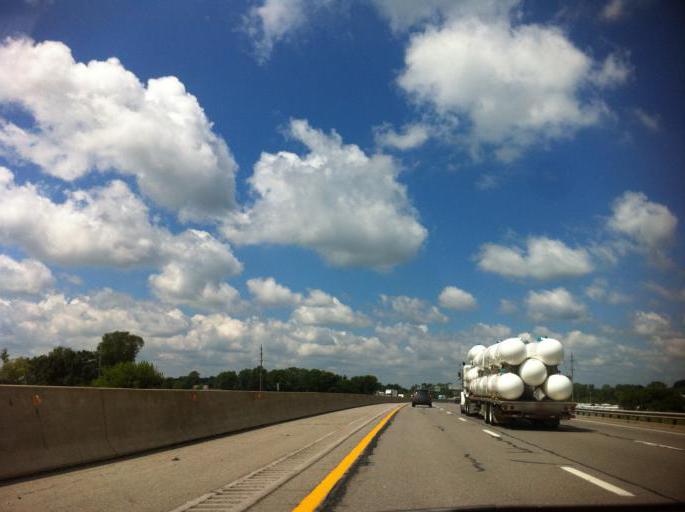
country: US
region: Ohio
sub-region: Erie County
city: Milan
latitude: 41.3231
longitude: -82.6178
